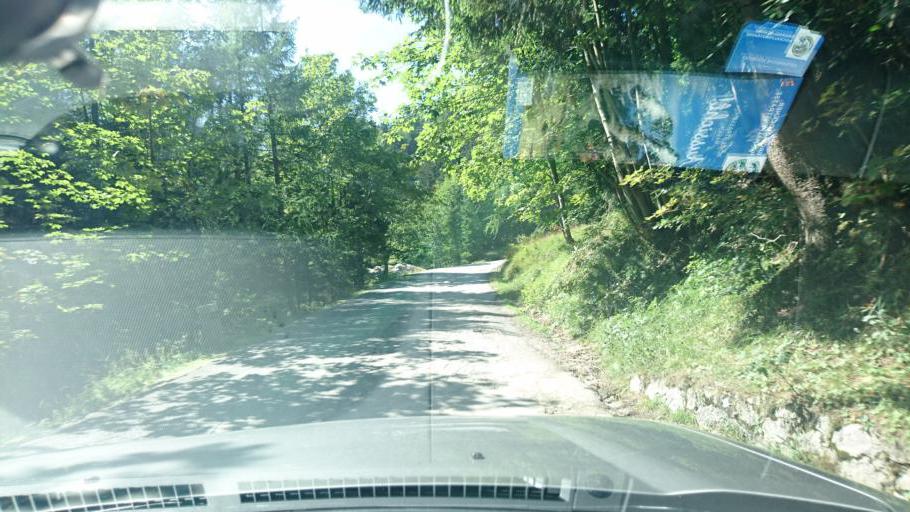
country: SI
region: Kranjska Gora
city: Kranjska Gora
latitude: 46.4390
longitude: 13.7627
